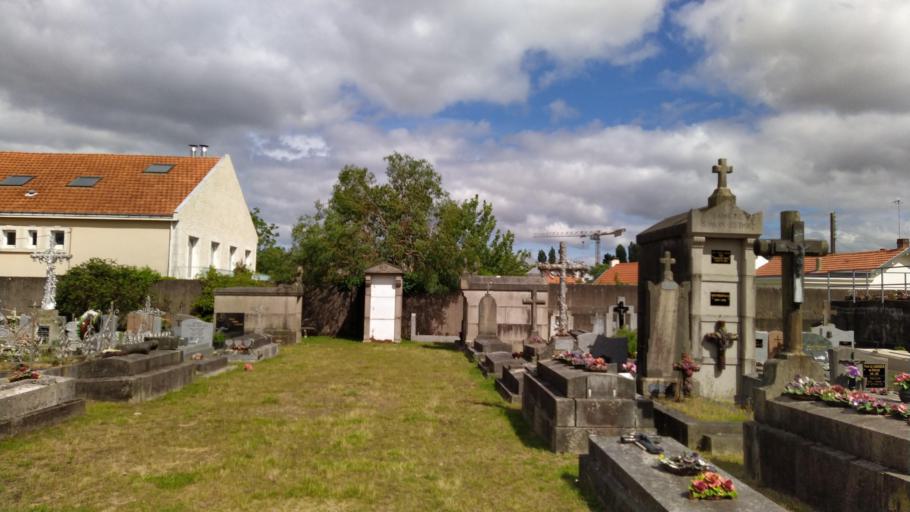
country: FR
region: Pays de la Loire
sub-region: Departement de la Loire-Atlantique
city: Nantes
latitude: 47.2158
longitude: -1.5929
